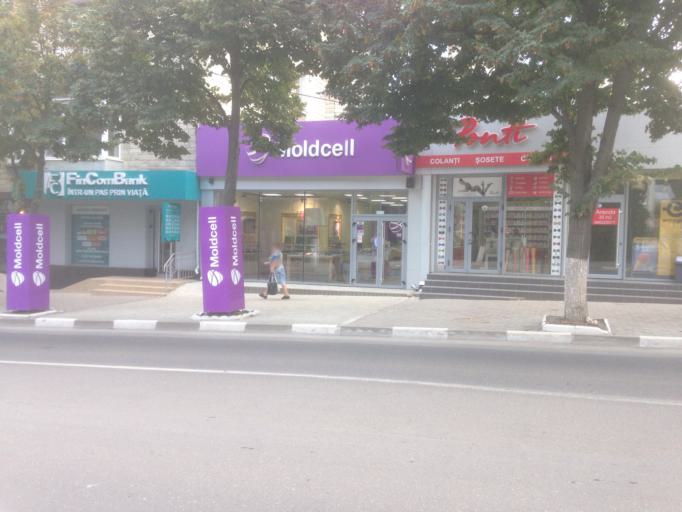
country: MD
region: Balti
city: Balti
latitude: 47.7630
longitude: 27.9287
